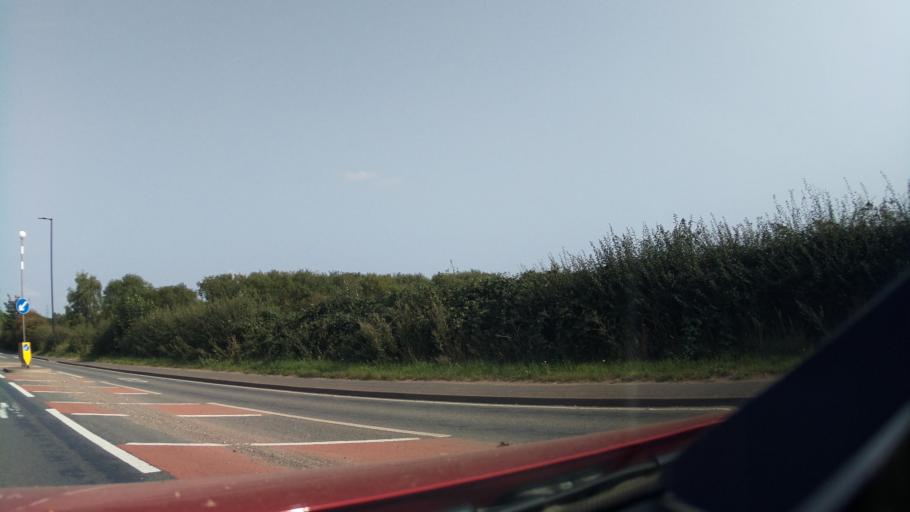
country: GB
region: England
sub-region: Walsall
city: Streetly
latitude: 52.5937
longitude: -1.8904
